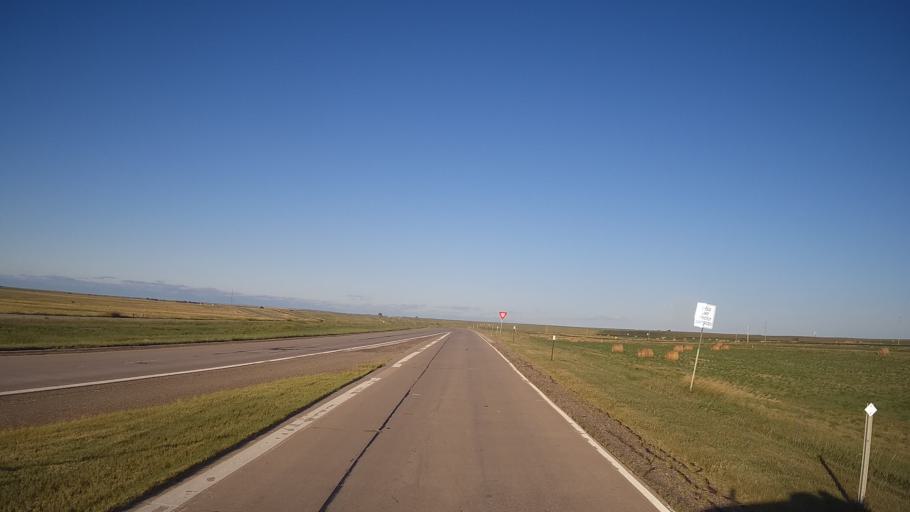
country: US
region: South Dakota
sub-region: Jackson County
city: Kadoka
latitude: 43.8425
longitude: -101.2280
